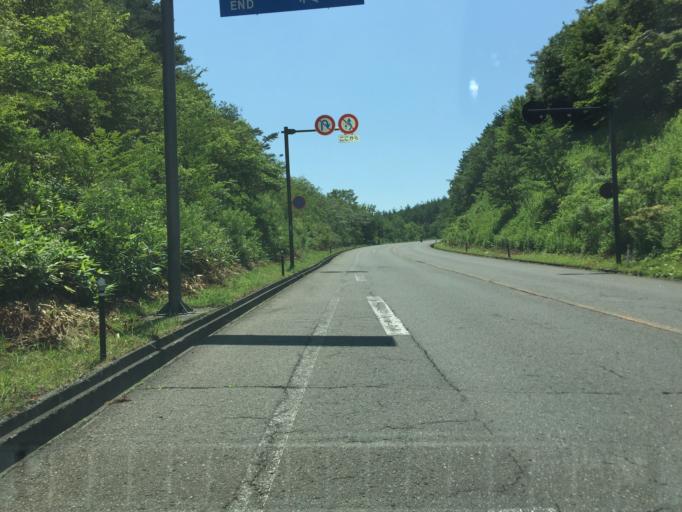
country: JP
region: Fukushima
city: Nihommatsu
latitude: 37.6658
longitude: 140.3282
